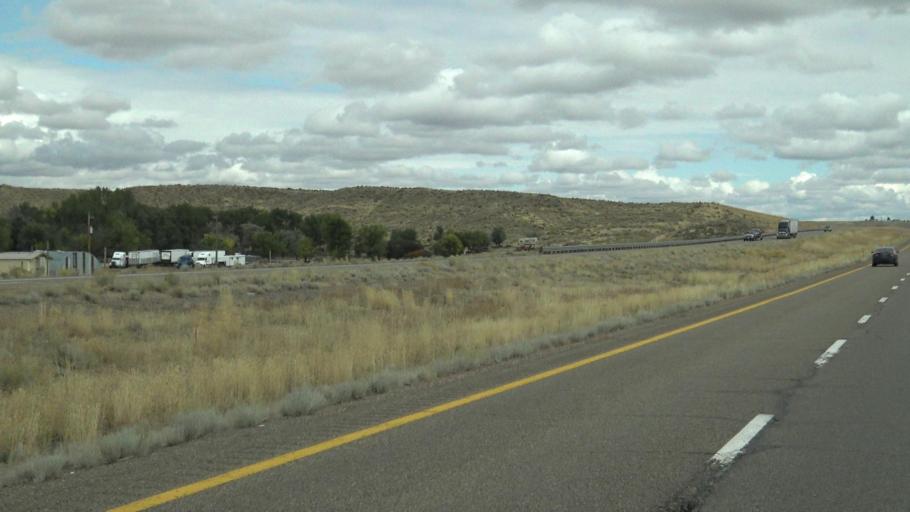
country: US
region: Nevada
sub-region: Elko County
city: Elko
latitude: 40.9050
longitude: -115.7006
